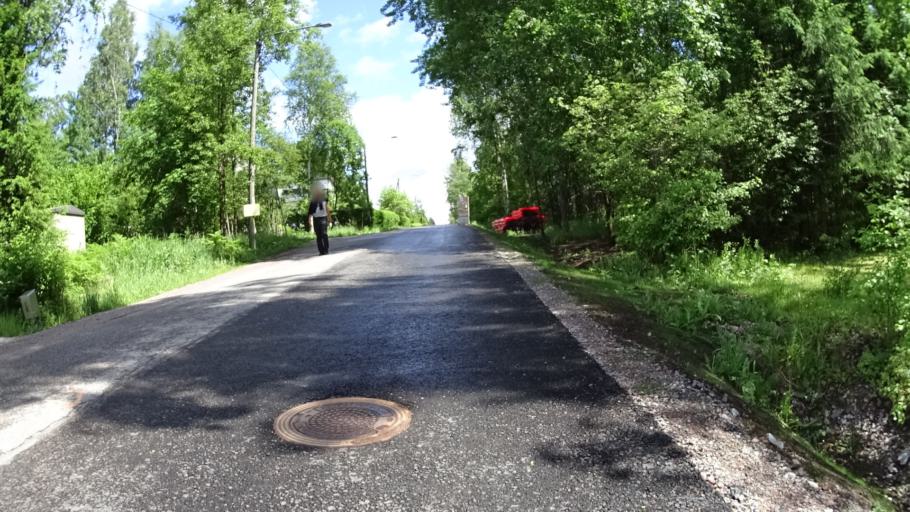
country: FI
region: Uusimaa
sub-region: Helsinki
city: Kilo
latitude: 60.2399
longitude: 24.8016
